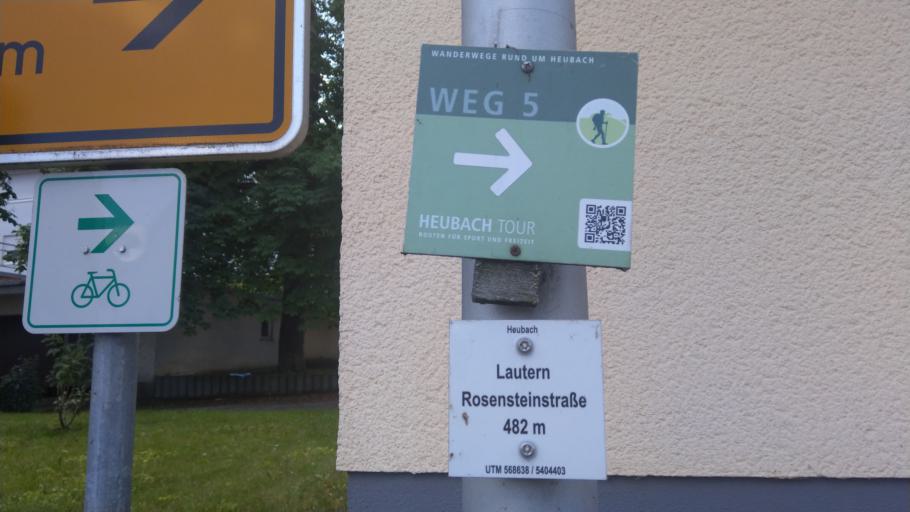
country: DE
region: Baden-Wuerttemberg
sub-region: Regierungsbezirk Stuttgart
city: Mogglingen
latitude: 48.8004
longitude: 9.9729
